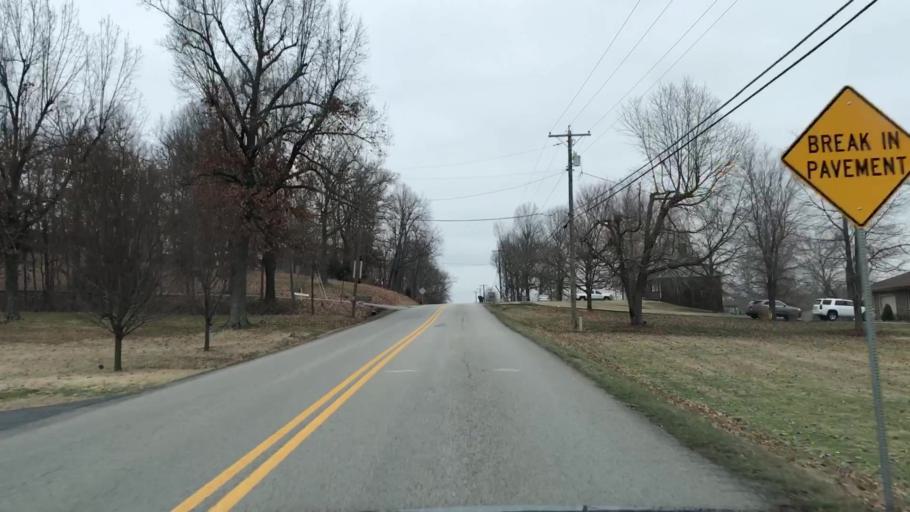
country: US
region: Kentucky
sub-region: Muhlenberg County
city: Greenville
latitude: 37.2253
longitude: -87.1936
